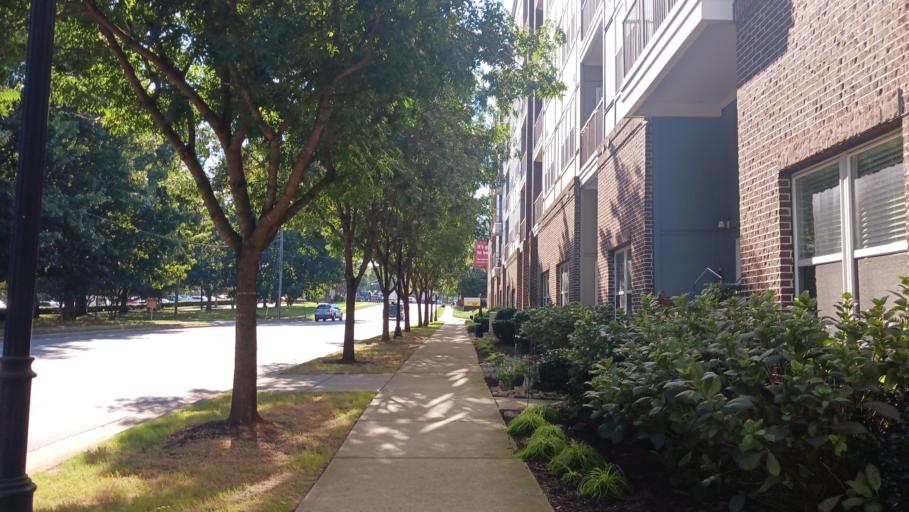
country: US
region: North Carolina
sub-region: Mecklenburg County
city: Charlotte
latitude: 35.2152
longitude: -80.8329
